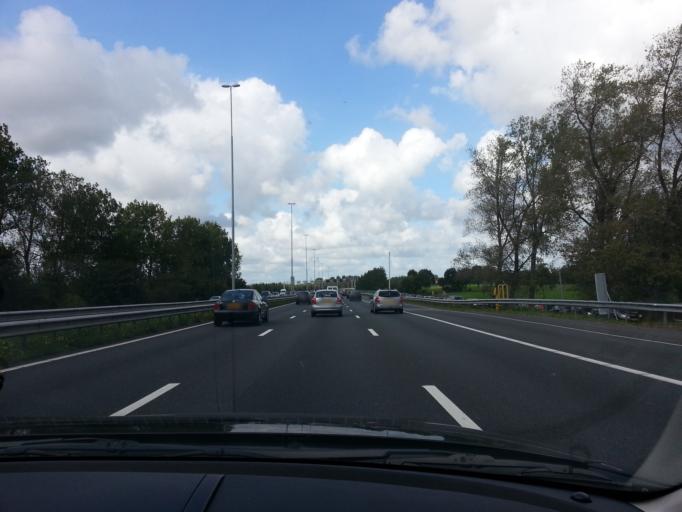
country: NL
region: South Holland
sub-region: Gemeente Schiedam
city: Schiedam
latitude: 51.9675
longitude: 4.4028
